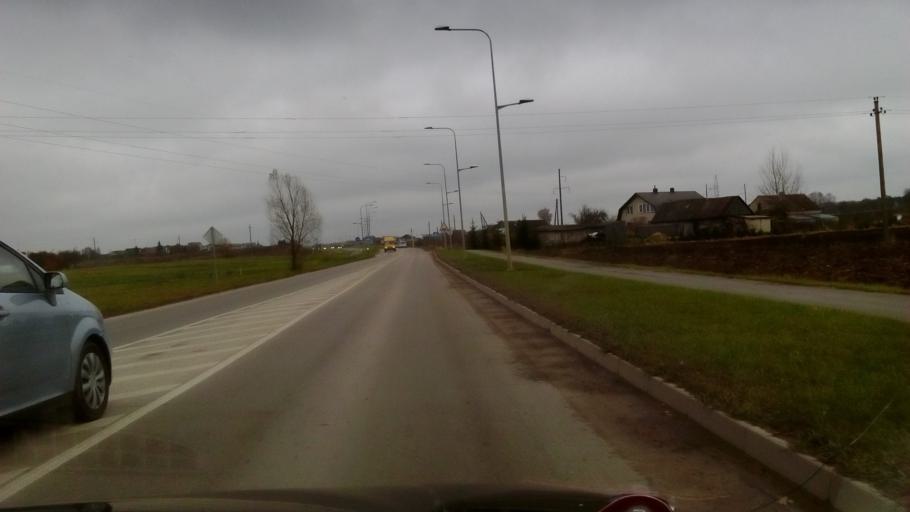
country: LT
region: Marijampoles apskritis
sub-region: Marijampole Municipality
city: Marijampole
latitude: 54.5321
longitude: 23.3613
